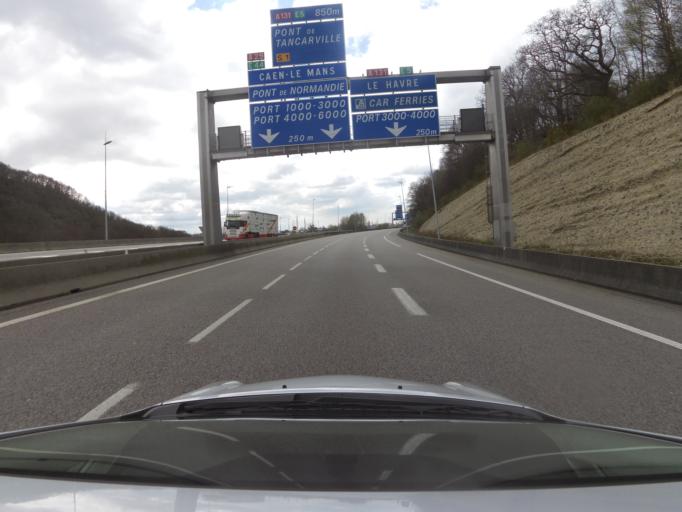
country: FR
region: Haute-Normandie
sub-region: Departement de la Seine-Maritime
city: Rogerville
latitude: 49.4999
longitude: 0.2750
